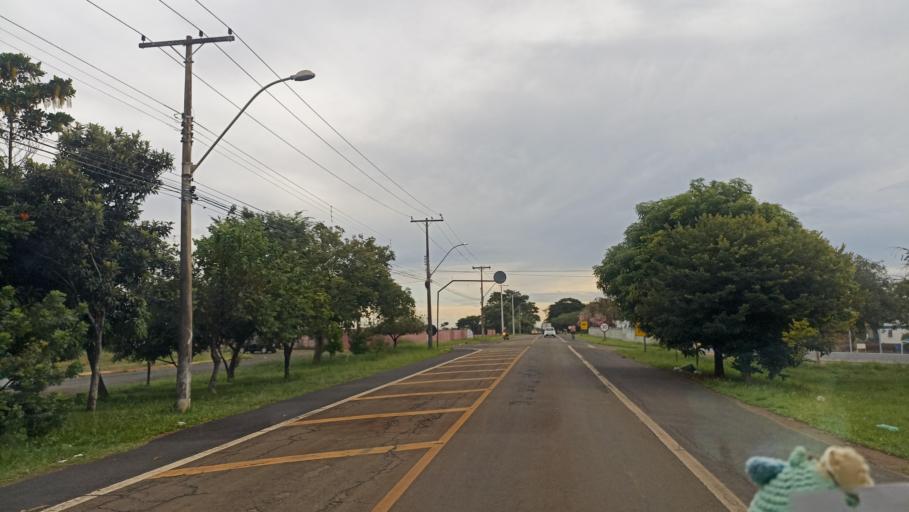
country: BR
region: Sao Paulo
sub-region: Jaboticabal
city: Jaboticabal
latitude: -21.2604
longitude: -48.3316
